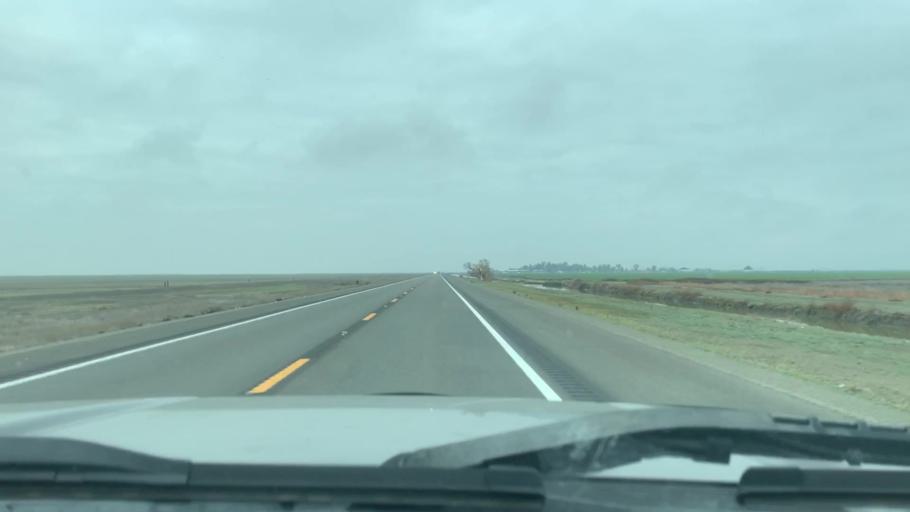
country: US
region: California
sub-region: Kings County
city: Stratford
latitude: 36.1072
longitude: -119.9024
